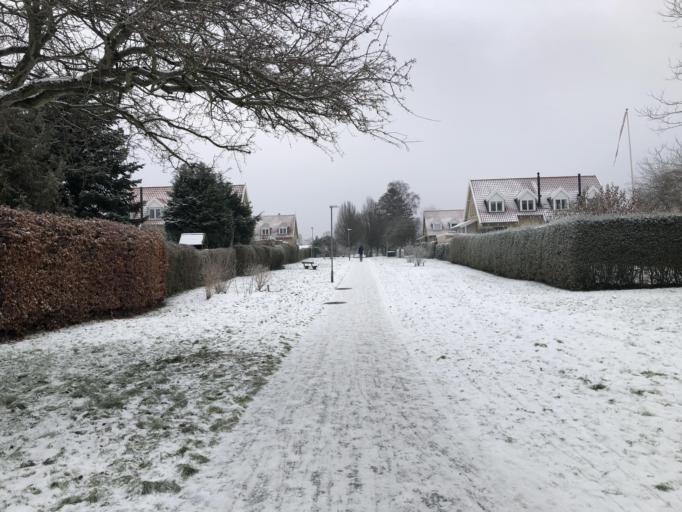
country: DK
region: Capital Region
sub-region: Rudersdal Kommune
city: Holte
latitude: 55.7853
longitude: 12.4624
